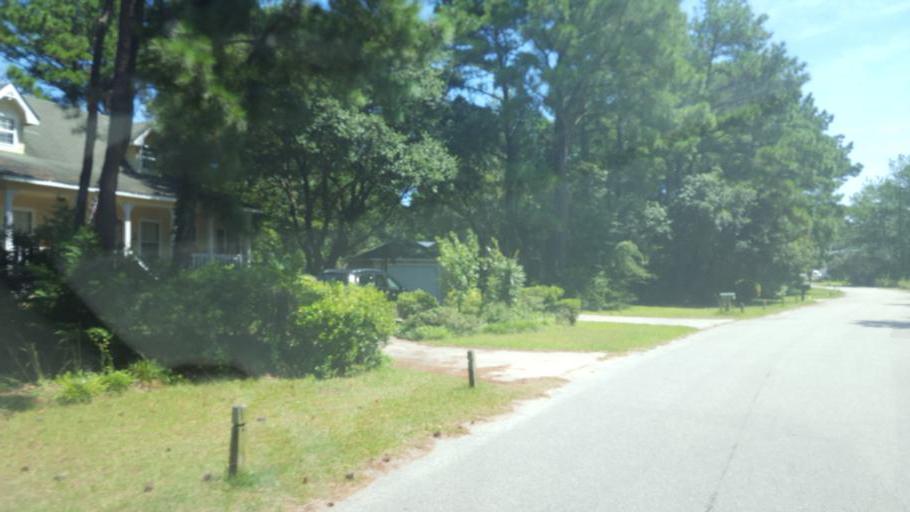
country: US
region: North Carolina
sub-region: Dare County
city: Kill Devil Hills
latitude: 35.9965
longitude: -75.6576
